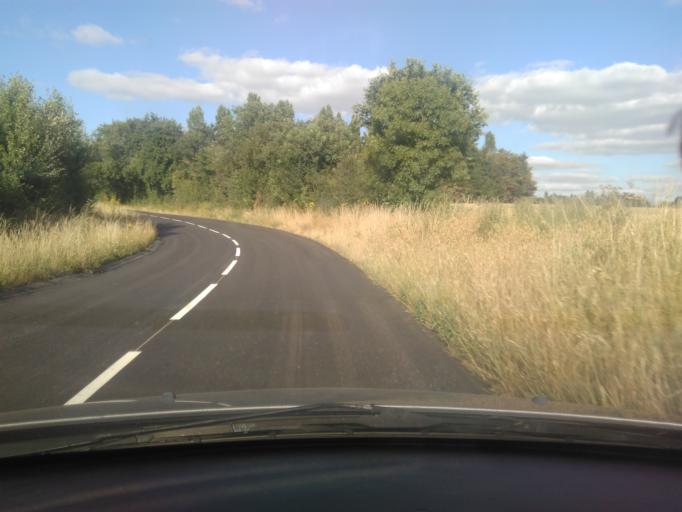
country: FR
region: Pays de la Loire
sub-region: Departement de la Vendee
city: Saint-Florent-des-Bois
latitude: 46.5785
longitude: -1.3260
